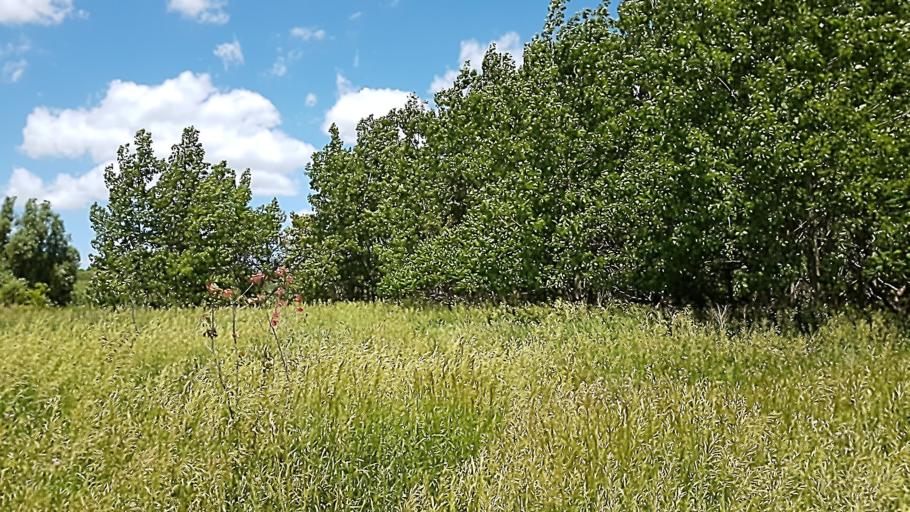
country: CA
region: Ontario
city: Scarborough
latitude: 43.7076
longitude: -79.2381
